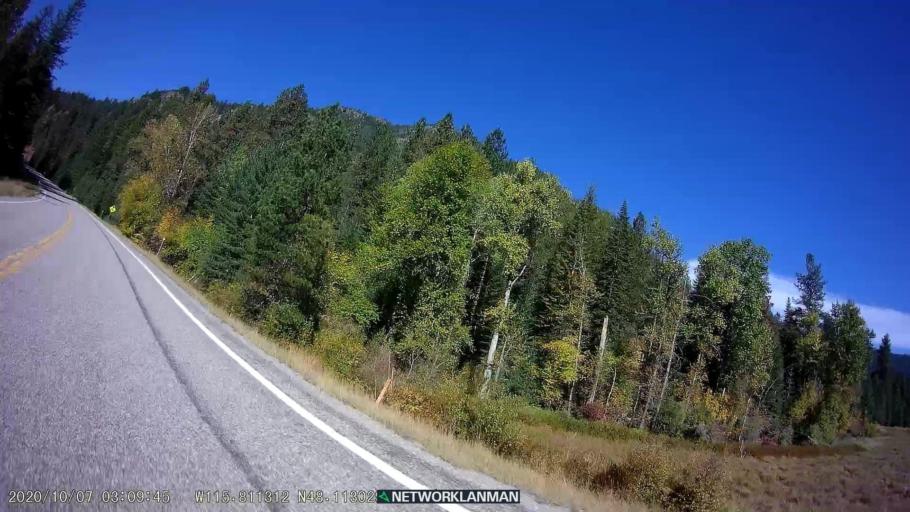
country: US
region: Montana
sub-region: Lincoln County
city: Libby
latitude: 48.1133
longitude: -115.8120
